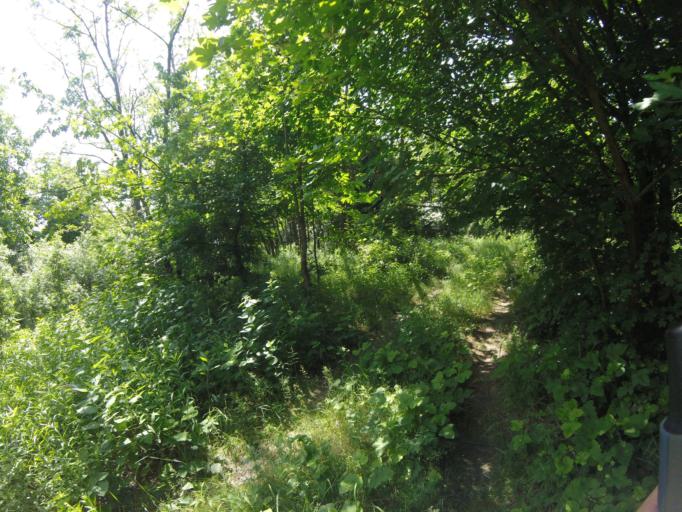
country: HU
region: Zala
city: Zalaszentgrot
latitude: 46.9029
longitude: 17.0377
